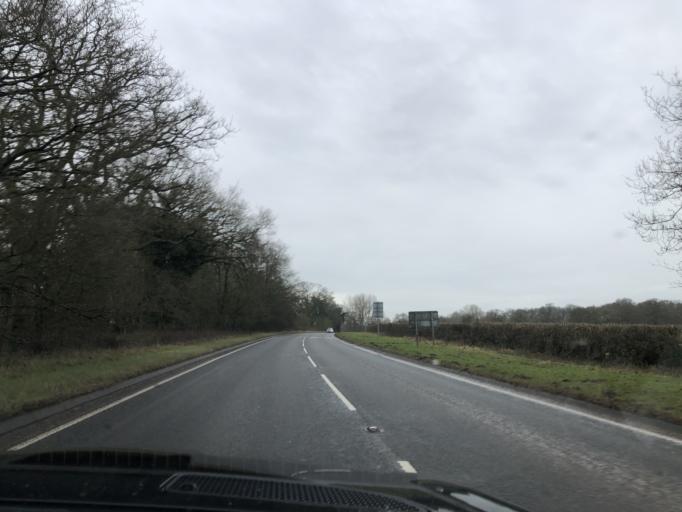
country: GB
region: England
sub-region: Warwickshire
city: Wroxall
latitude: 52.3341
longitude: -1.6605
